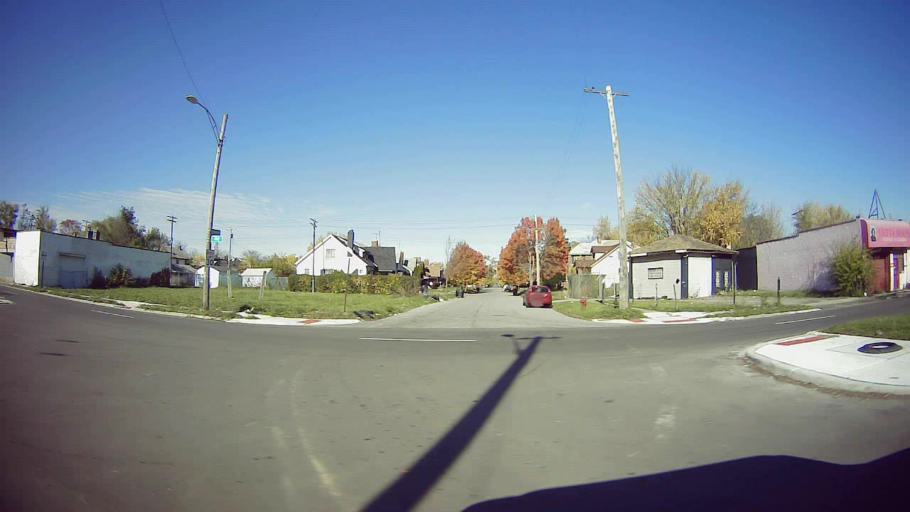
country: US
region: Michigan
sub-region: Wayne County
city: Dearborn
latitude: 42.3587
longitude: -83.1641
